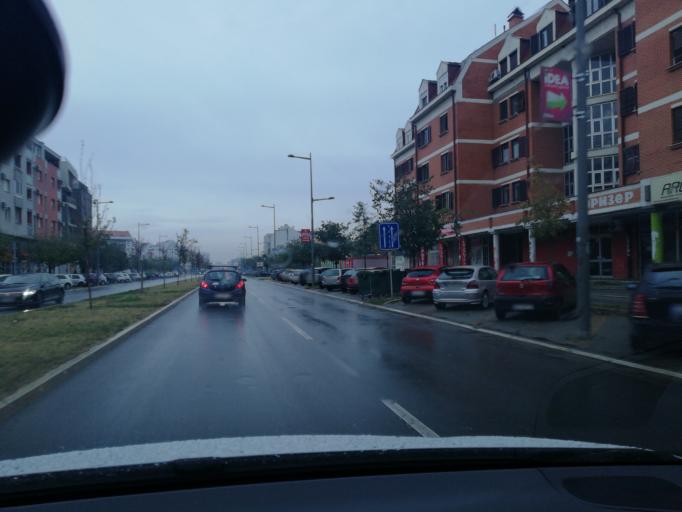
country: RS
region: Autonomna Pokrajina Vojvodina
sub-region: Juznobacki Okrug
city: Novi Sad
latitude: 45.2410
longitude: 19.8080
